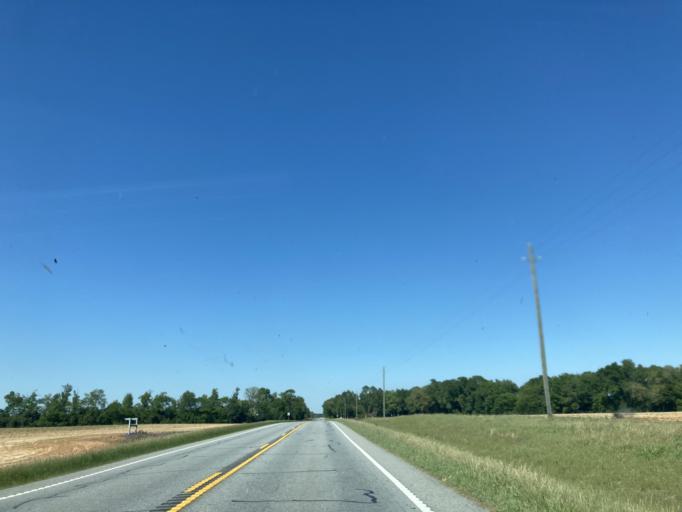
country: US
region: Georgia
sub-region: Baker County
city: Newton
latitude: 31.2244
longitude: -84.4458
